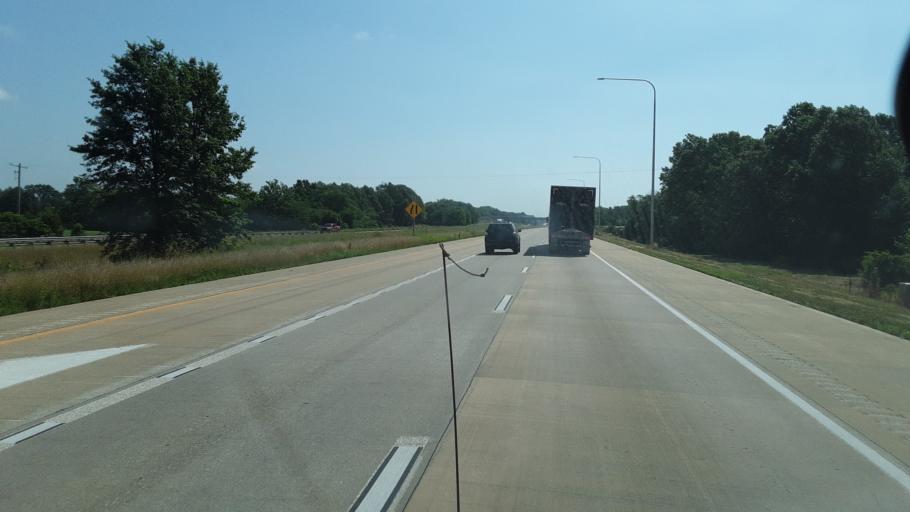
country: US
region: Illinois
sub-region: Effingham County
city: Teutopolis
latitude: 39.1500
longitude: -88.5018
